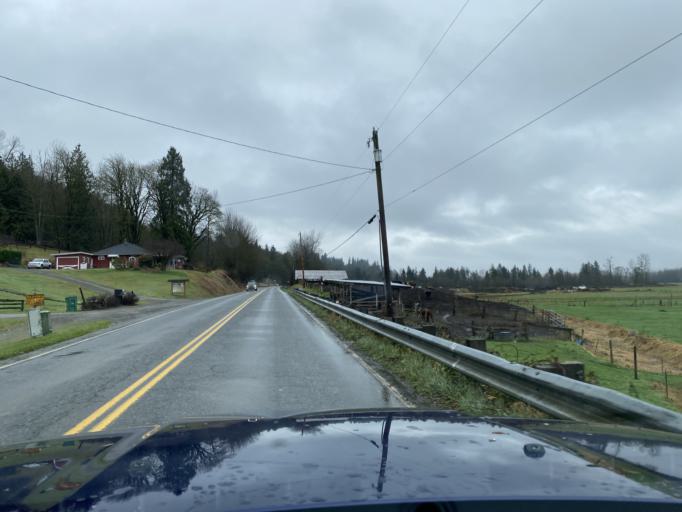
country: US
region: Washington
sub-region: King County
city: Duvall
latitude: 47.7671
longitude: -122.0009
